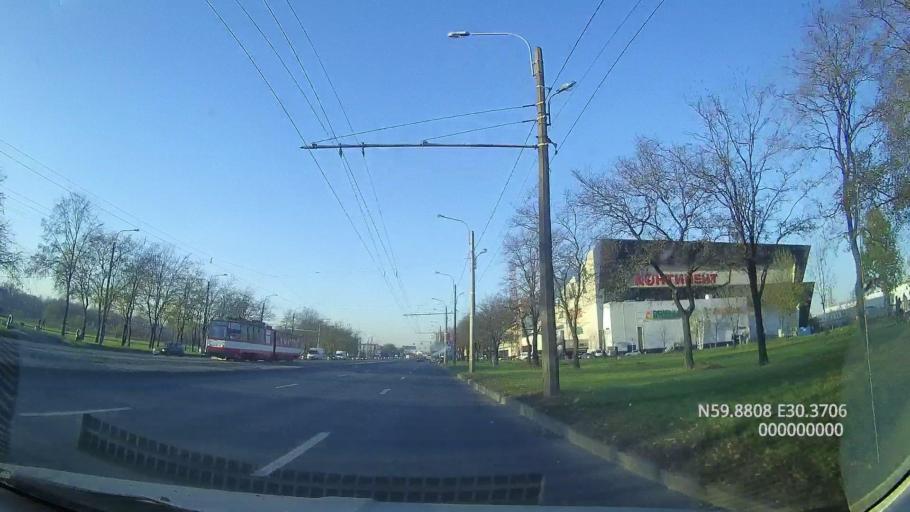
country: RU
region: St.-Petersburg
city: Kupchino
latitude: 59.8809
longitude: 30.3713
